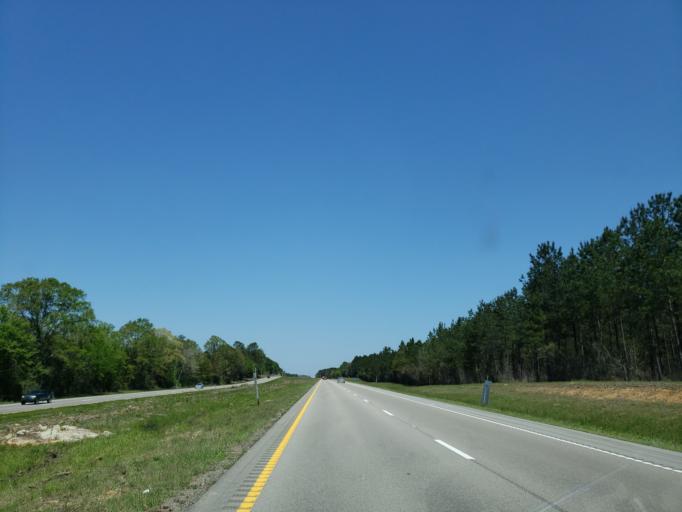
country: US
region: Mississippi
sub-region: Stone County
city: Wiggins
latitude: 30.9956
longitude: -89.2011
